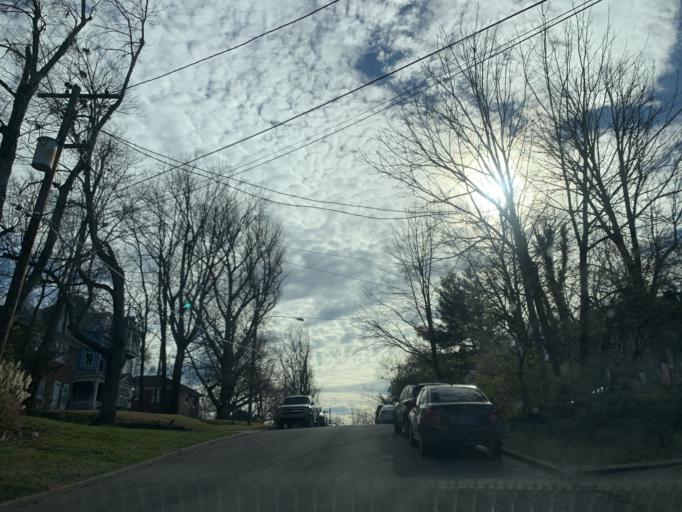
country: US
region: Kentucky
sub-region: Jefferson County
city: Indian Hills
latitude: 38.2515
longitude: -85.6995
